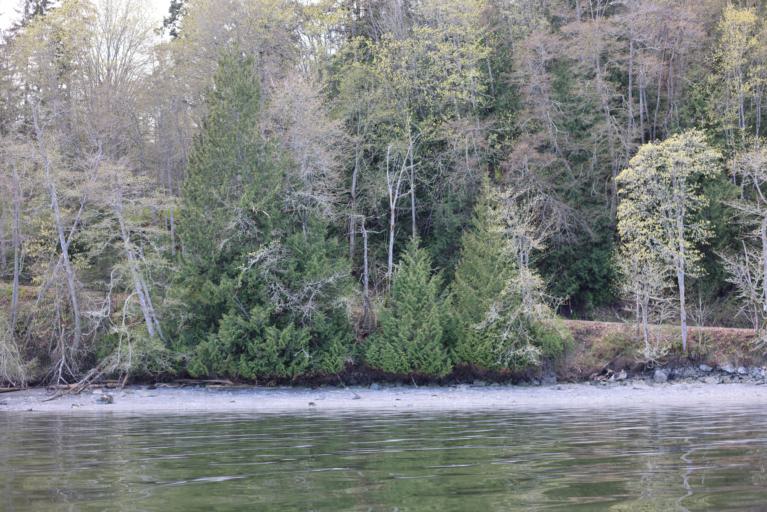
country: CA
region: British Columbia
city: North Saanich
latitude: 48.6198
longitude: -123.5219
